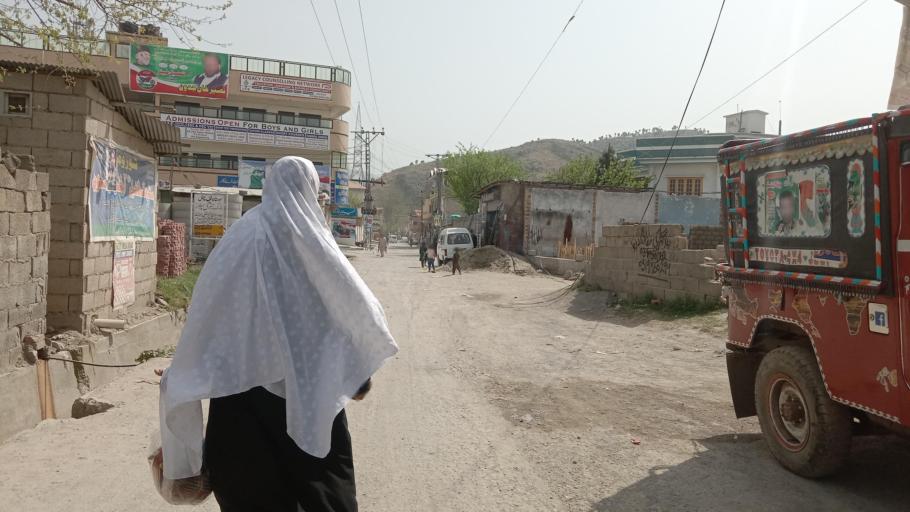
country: PK
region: Khyber Pakhtunkhwa
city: Abbottabad
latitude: 34.1573
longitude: 73.2594
